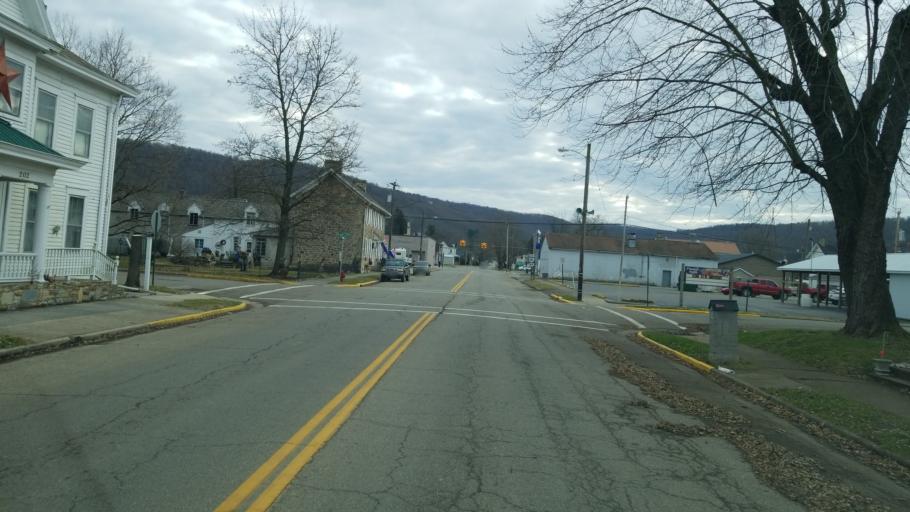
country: US
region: Ohio
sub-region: Highland County
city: Greenfield
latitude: 39.2292
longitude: -83.2706
